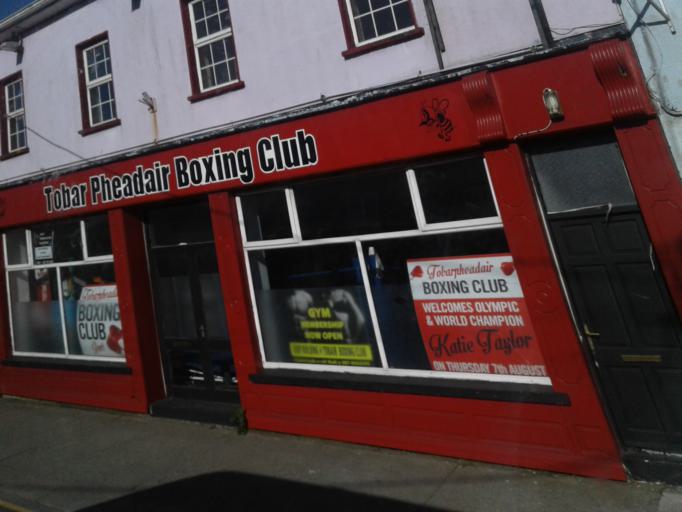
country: IE
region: Connaught
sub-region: County Galway
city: Gort
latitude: 53.0681
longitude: -8.8197
